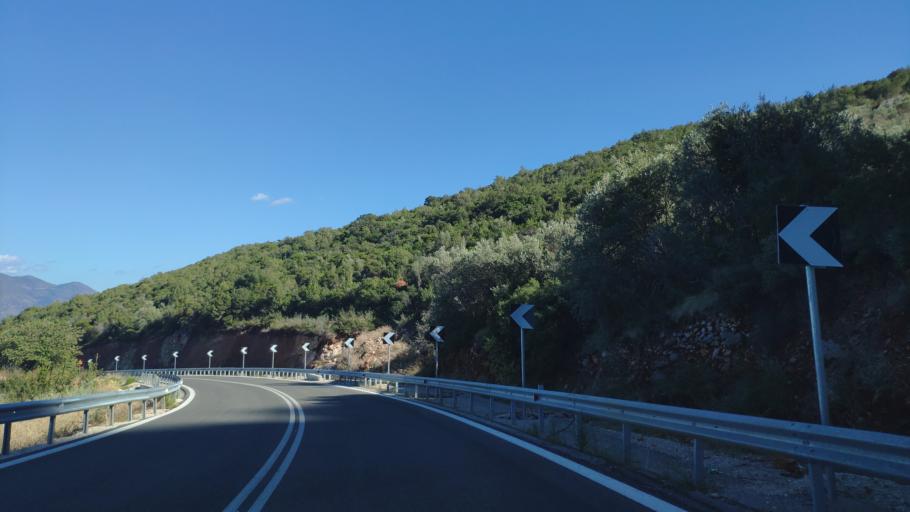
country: GR
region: Peloponnese
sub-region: Nomos Argolidos
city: Didyma
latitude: 37.5534
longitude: 23.2668
